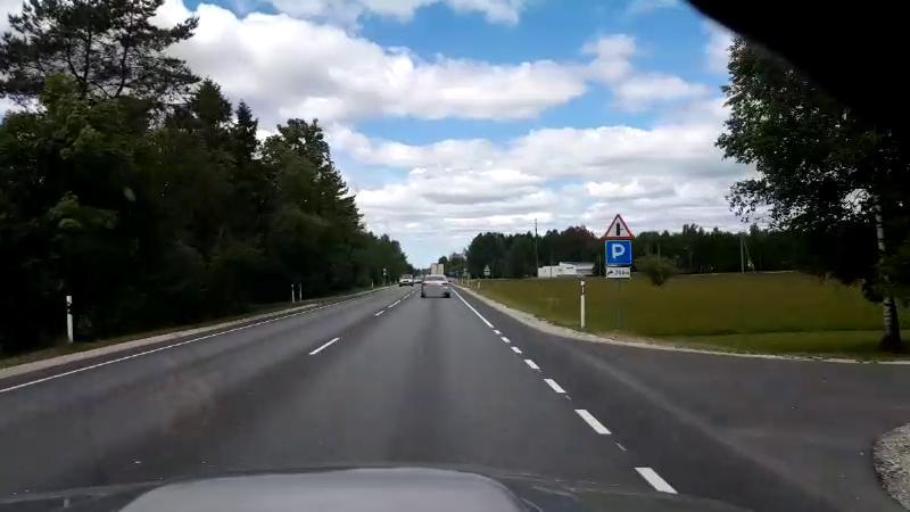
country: EE
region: Paernumaa
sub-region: Halinga vald
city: Parnu-Jaagupi
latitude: 58.6562
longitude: 24.4740
